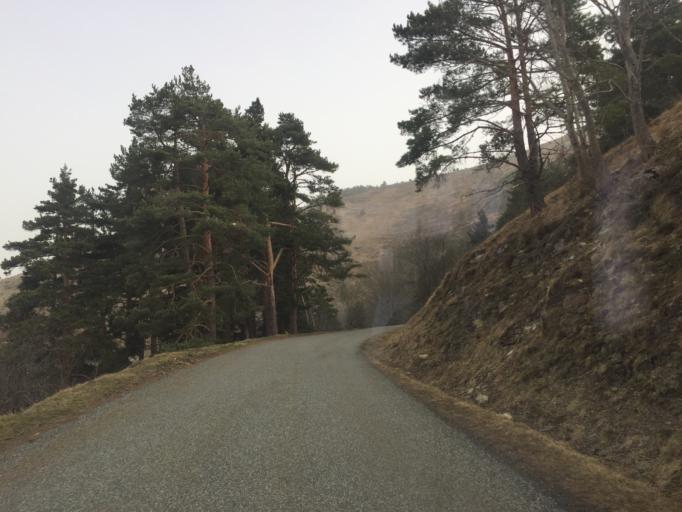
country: FR
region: Midi-Pyrenees
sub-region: Departement des Hautes-Pyrenees
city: Saint-Lary-Soulan
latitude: 42.8168
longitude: 0.3525
